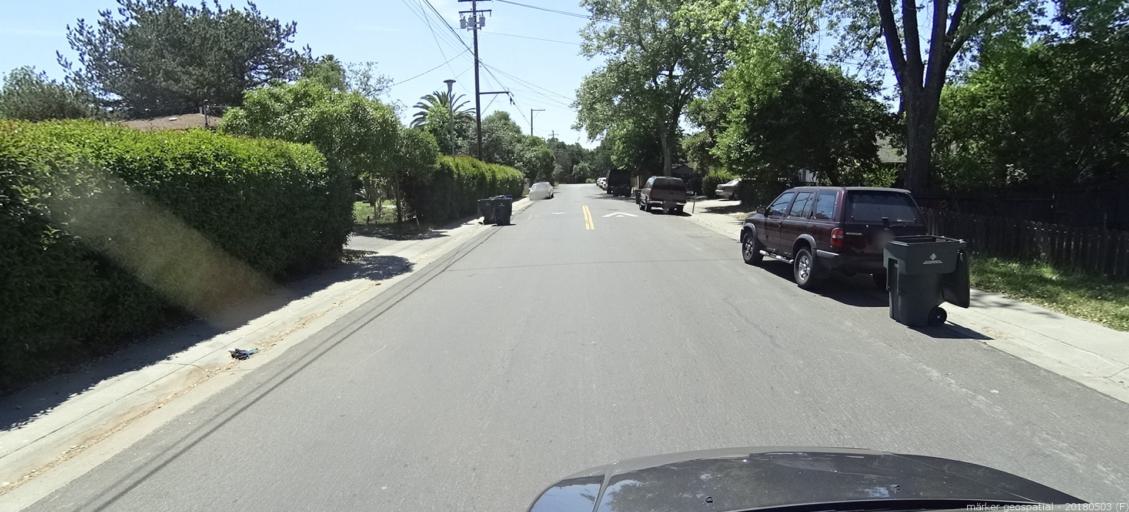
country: US
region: California
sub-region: Sacramento County
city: Arden-Arcade
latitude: 38.6322
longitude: -121.4183
